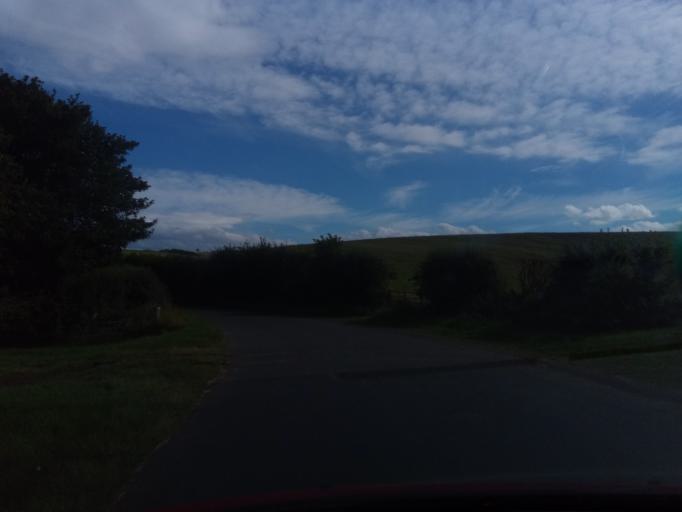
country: GB
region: Scotland
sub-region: The Scottish Borders
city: Coldstream
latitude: 55.6351
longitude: -2.1891
